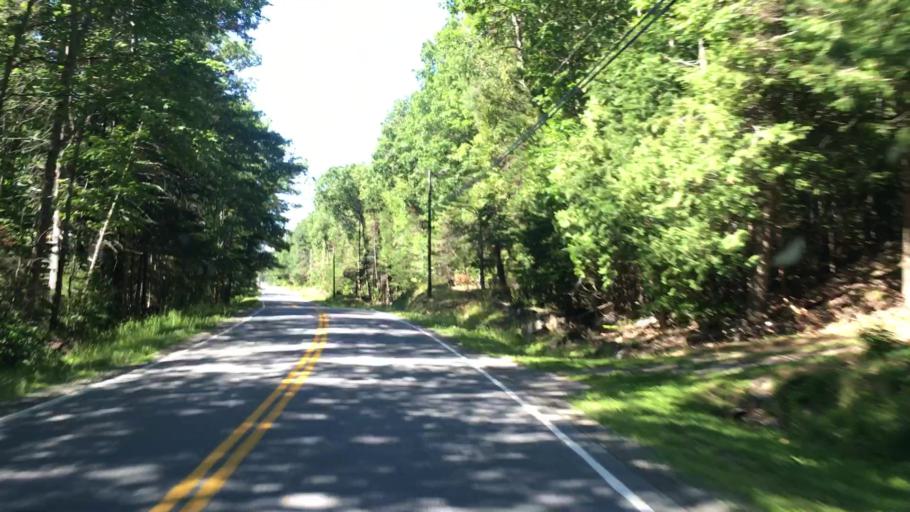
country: US
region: Maine
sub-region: Hancock County
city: Dedham
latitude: 44.7157
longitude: -68.6453
